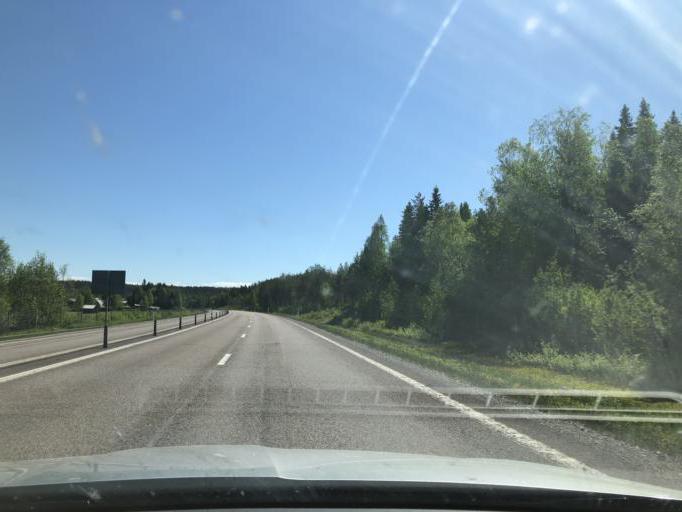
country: SE
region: Norrbotten
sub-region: Kalix Kommun
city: Rolfs
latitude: 65.8826
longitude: 22.9336
